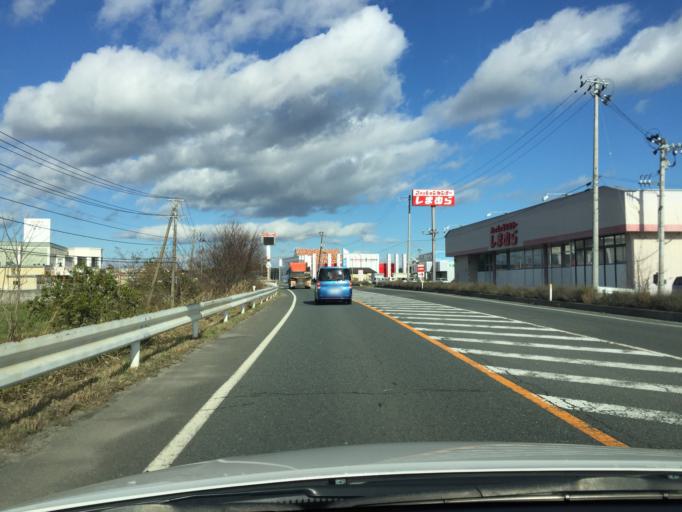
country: JP
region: Fukushima
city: Namie
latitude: 37.4873
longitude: 141.0054
